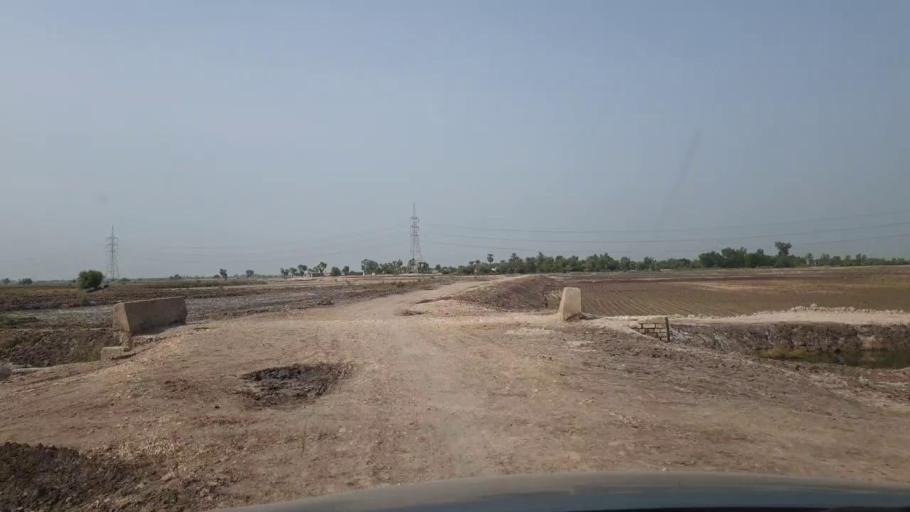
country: PK
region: Sindh
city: Lakhi
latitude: 27.8313
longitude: 68.6980
